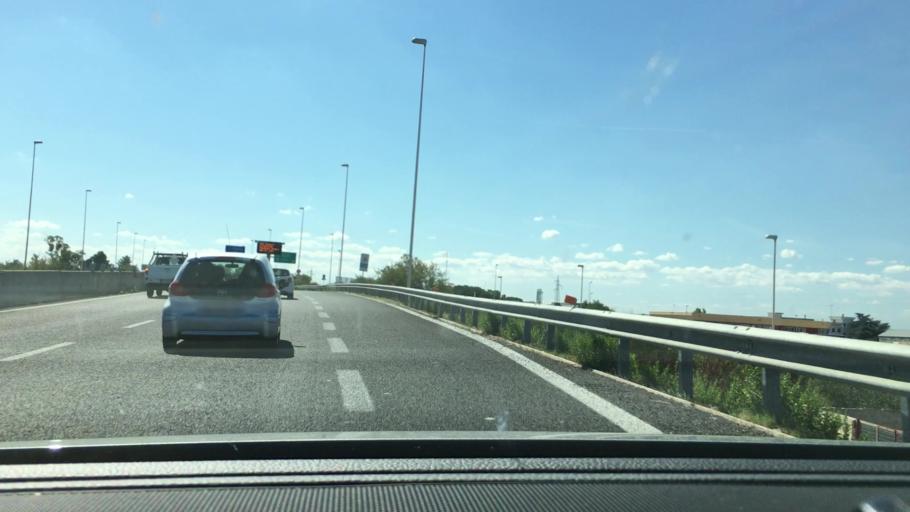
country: IT
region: Apulia
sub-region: Provincia di Bari
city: Bitritto
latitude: 41.0736
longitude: 16.8298
